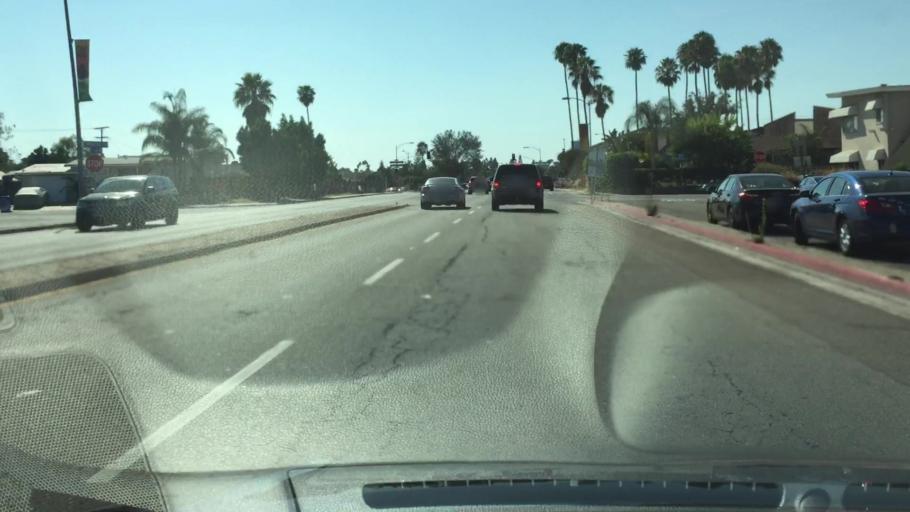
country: US
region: California
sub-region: San Diego County
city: Lemon Grove
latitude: 32.7453
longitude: -117.0569
